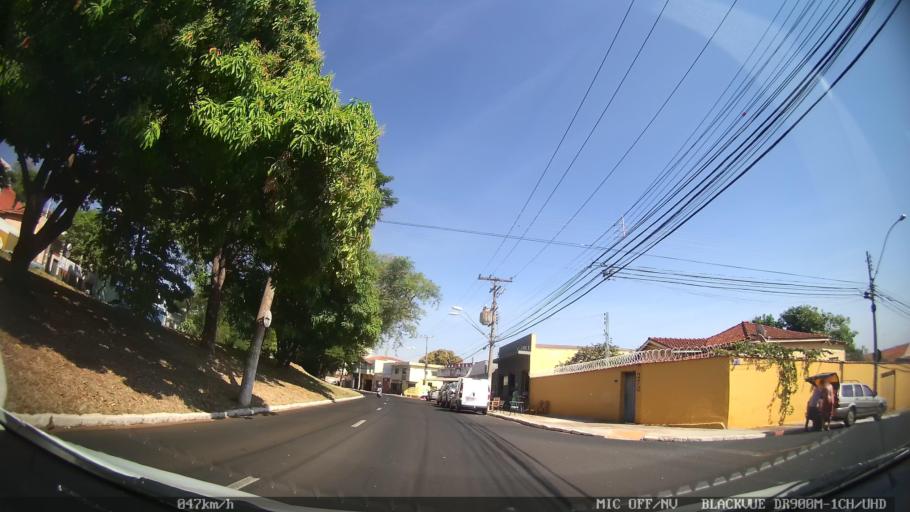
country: BR
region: Sao Paulo
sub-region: Ribeirao Preto
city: Ribeirao Preto
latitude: -21.1806
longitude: -47.8181
